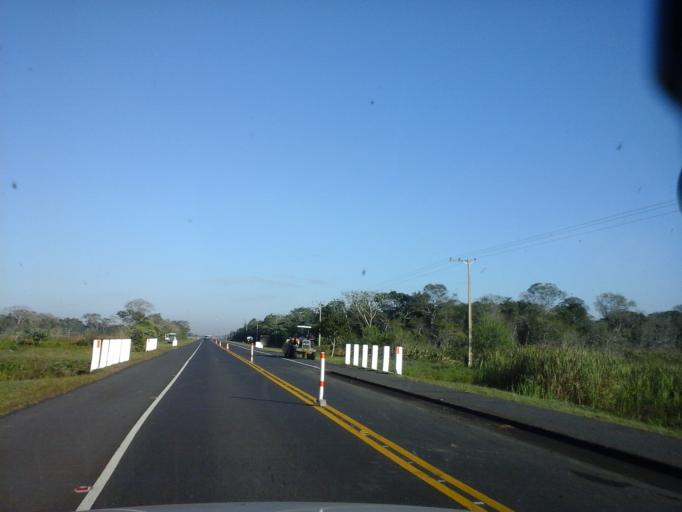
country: PY
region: Neembucu
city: Pilar
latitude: -26.8559
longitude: -57.9739
